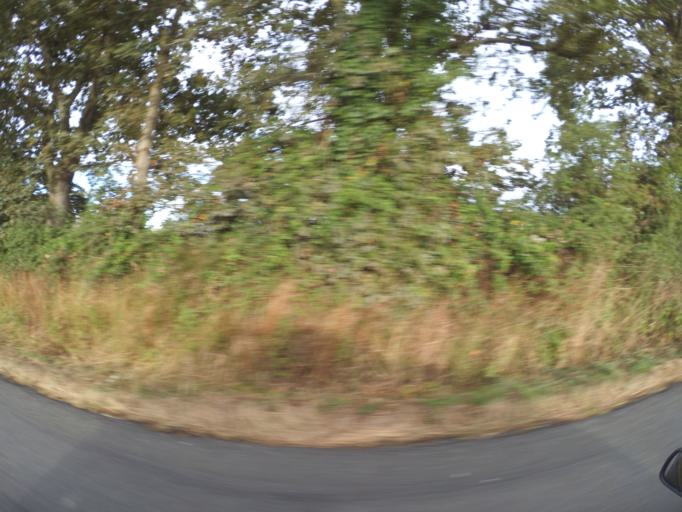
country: FR
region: Pays de la Loire
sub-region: Departement de la Loire-Atlantique
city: Vieillevigne
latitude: 46.9916
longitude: -1.4603
